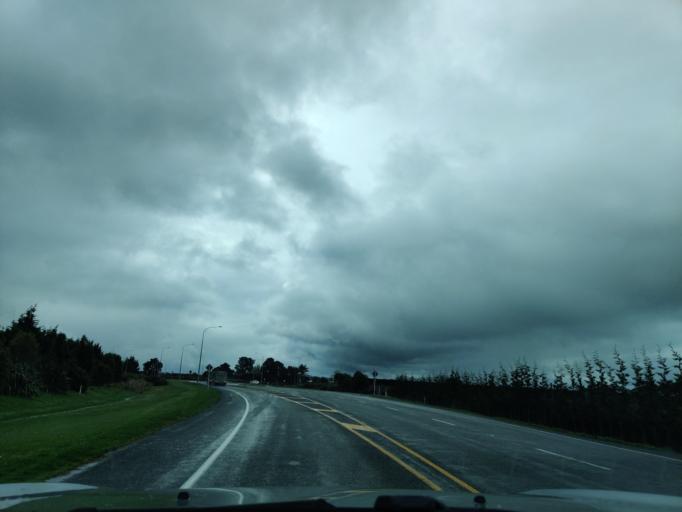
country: NZ
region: Hawke's Bay
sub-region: Hastings District
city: Hastings
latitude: -39.6606
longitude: 176.7939
